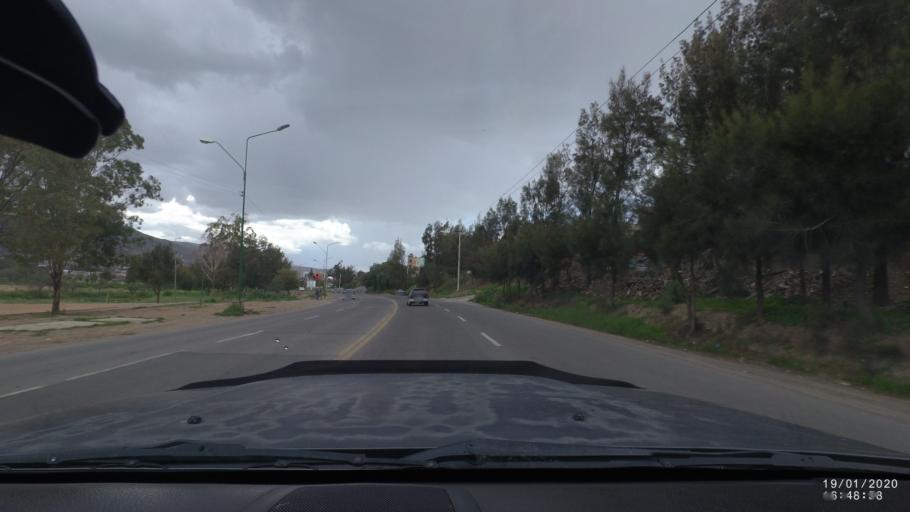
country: BO
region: Cochabamba
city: Cochabamba
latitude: -17.4147
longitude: -66.1422
